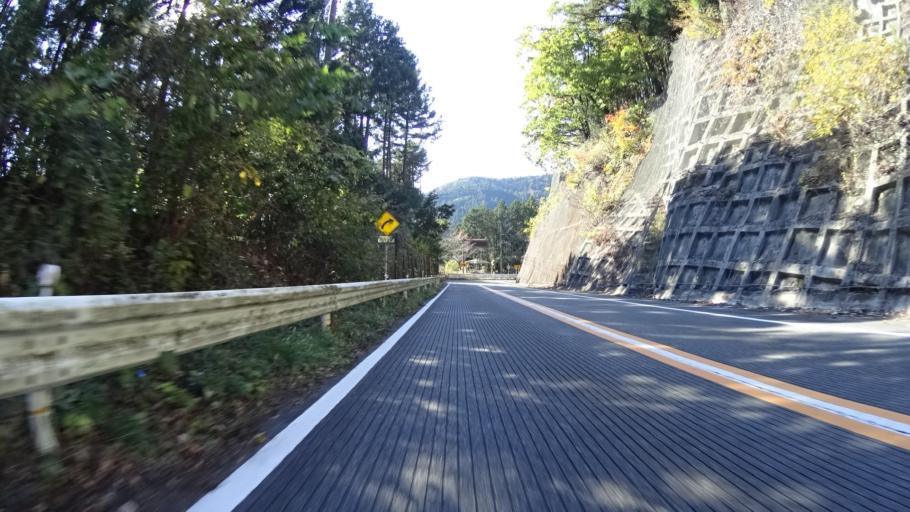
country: JP
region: Yamanashi
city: Uenohara
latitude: 35.6852
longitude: 139.1030
